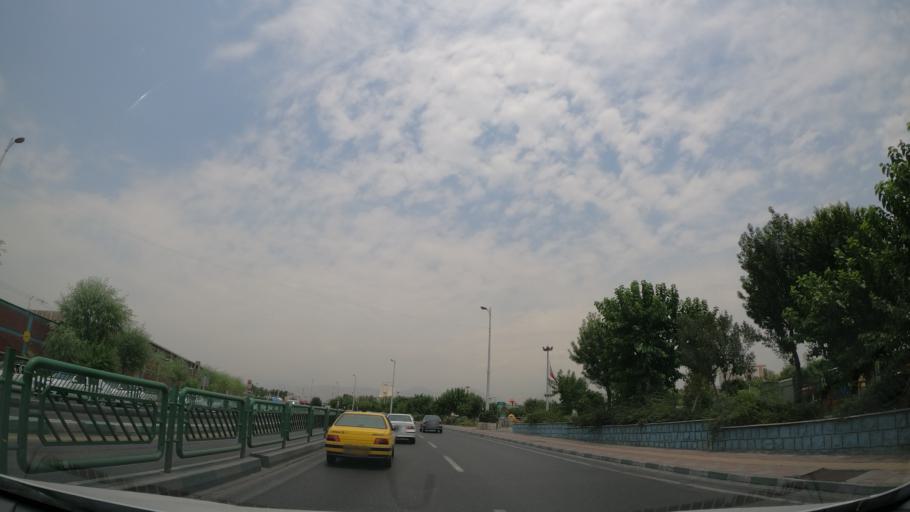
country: IR
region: Tehran
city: Tehran
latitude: 35.6950
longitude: 51.3400
